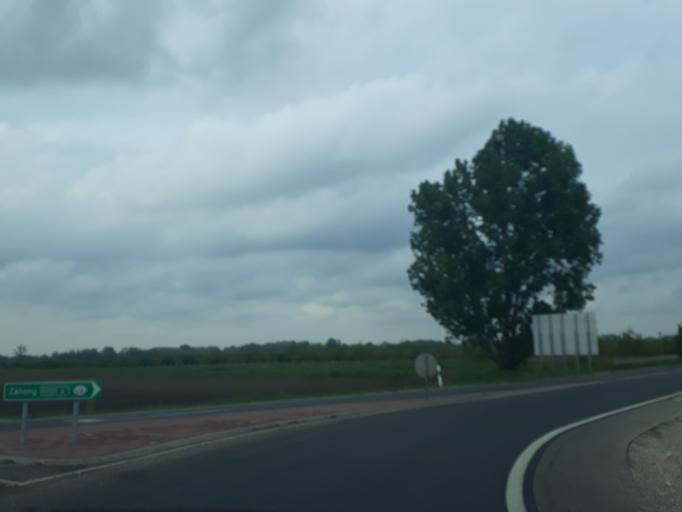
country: HU
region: Szabolcs-Szatmar-Bereg
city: Kisvarda
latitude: 48.2074
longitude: 22.0524
